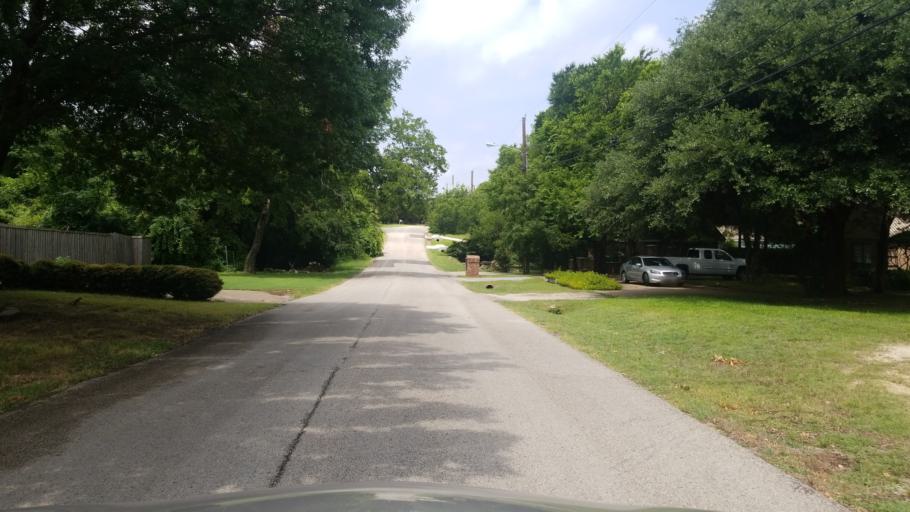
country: US
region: Texas
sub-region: Dallas County
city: Duncanville
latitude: 32.6776
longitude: -96.9307
